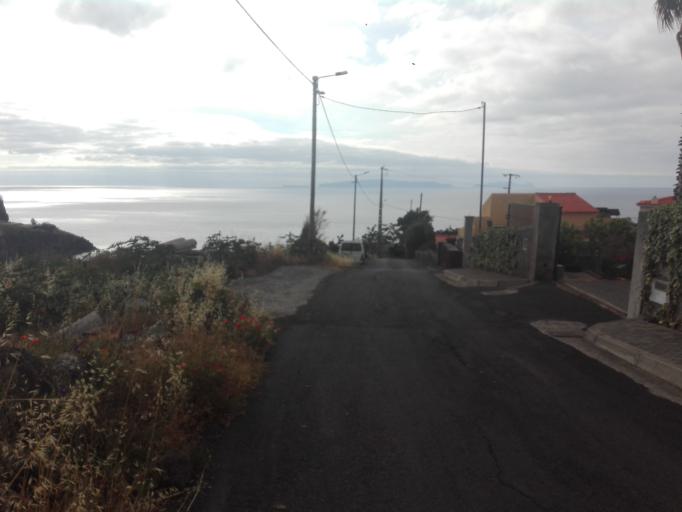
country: PT
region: Madeira
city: Canico
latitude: 32.6498
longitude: -16.8251
